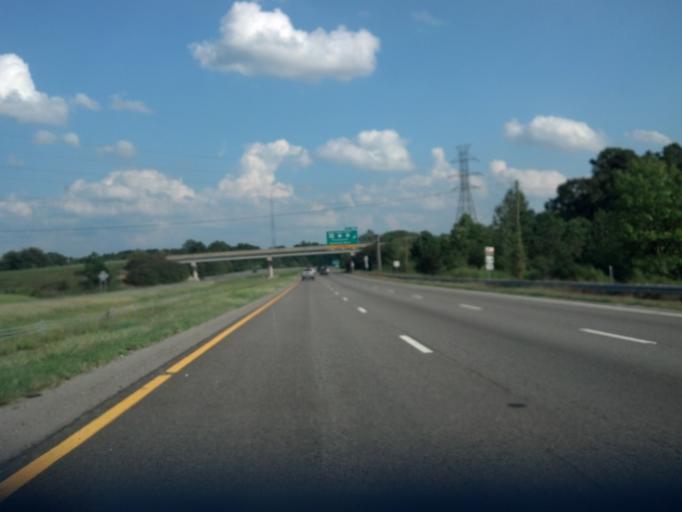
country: US
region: North Carolina
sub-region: Edgecombe County
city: Princeville
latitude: 35.8870
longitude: -77.5375
